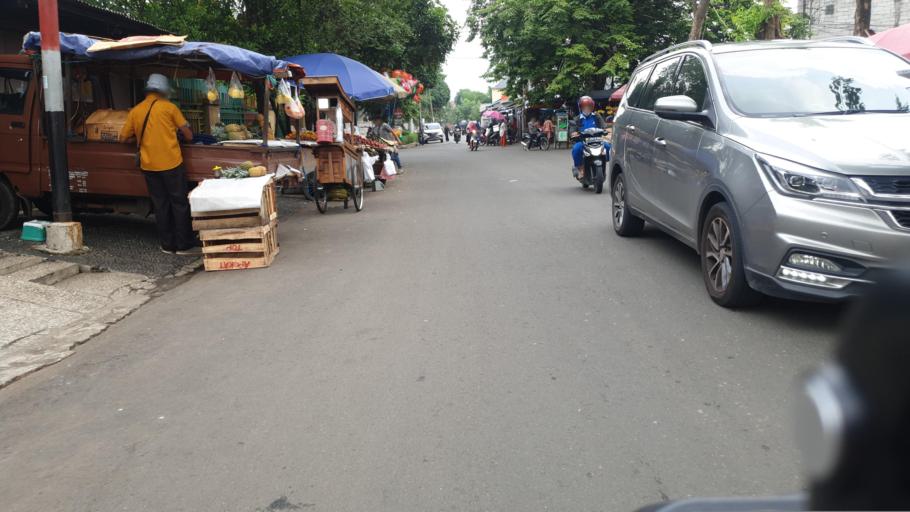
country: ID
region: West Java
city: Ciputat
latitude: -6.1955
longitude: 106.7514
